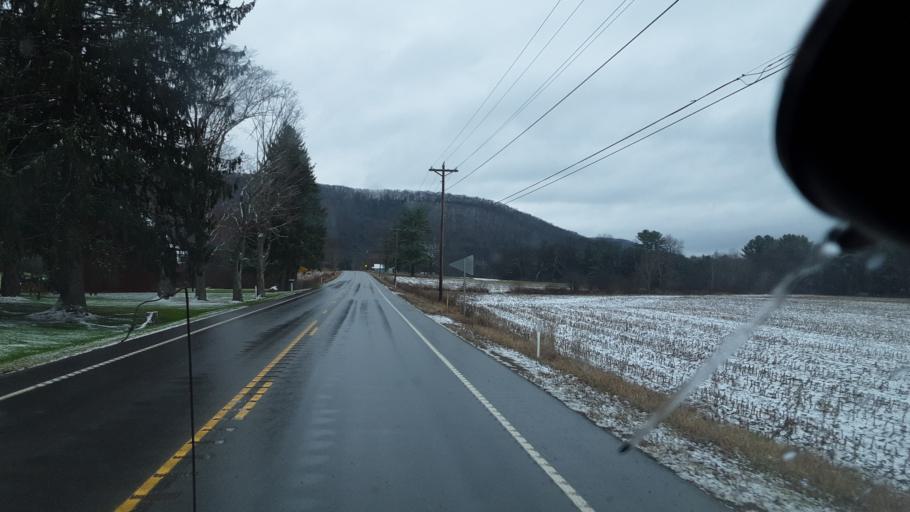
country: US
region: Pennsylvania
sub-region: Potter County
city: Shinglehouse
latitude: 41.9025
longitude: -78.0706
